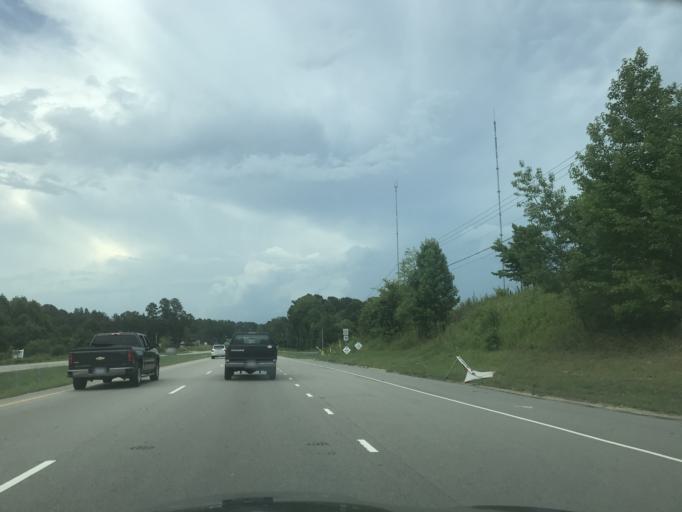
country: US
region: North Carolina
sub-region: Wake County
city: Garner
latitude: 35.6864
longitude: -78.5468
